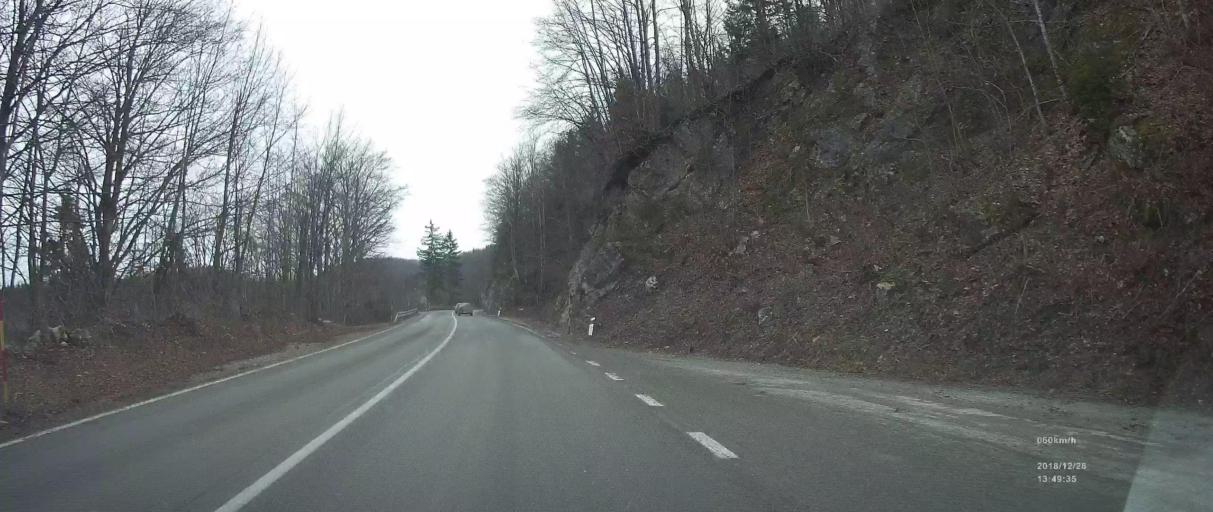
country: HR
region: Primorsko-Goranska
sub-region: Grad Delnice
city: Delnice
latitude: 45.3990
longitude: 14.8207
